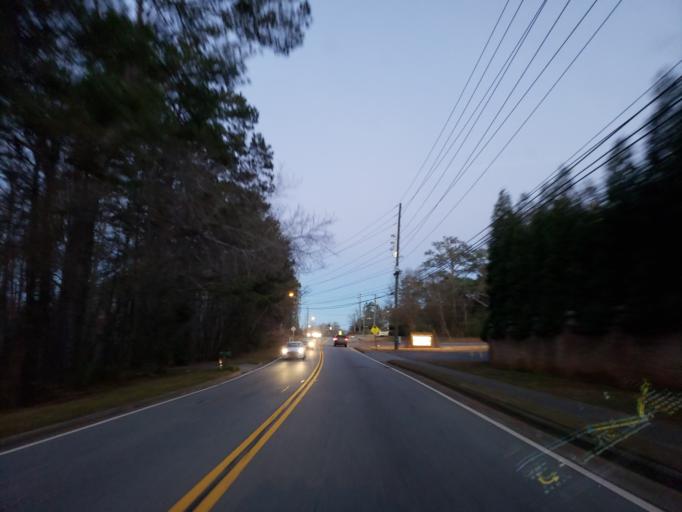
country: US
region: Georgia
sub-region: Cobb County
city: Kennesaw
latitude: 33.9659
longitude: -84.6709
